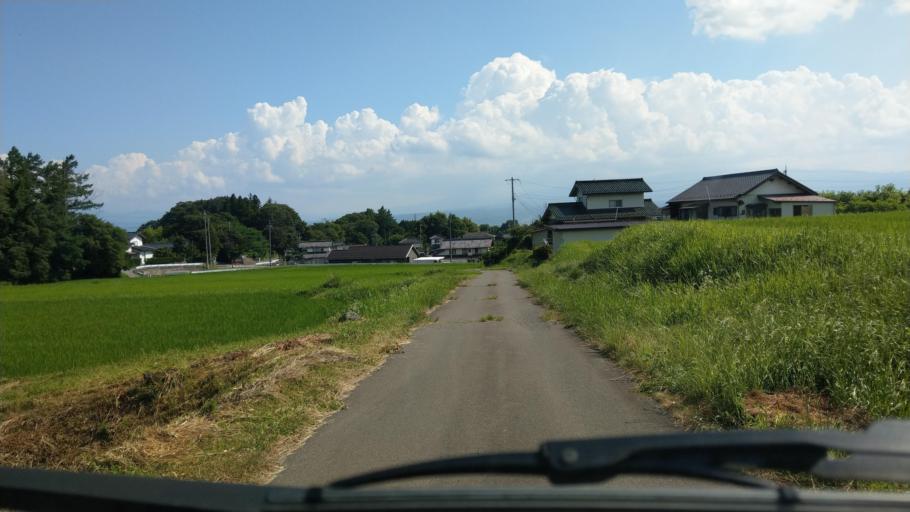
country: JP
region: Nagano
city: Komoro
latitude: 36.3242
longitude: 138.4498
